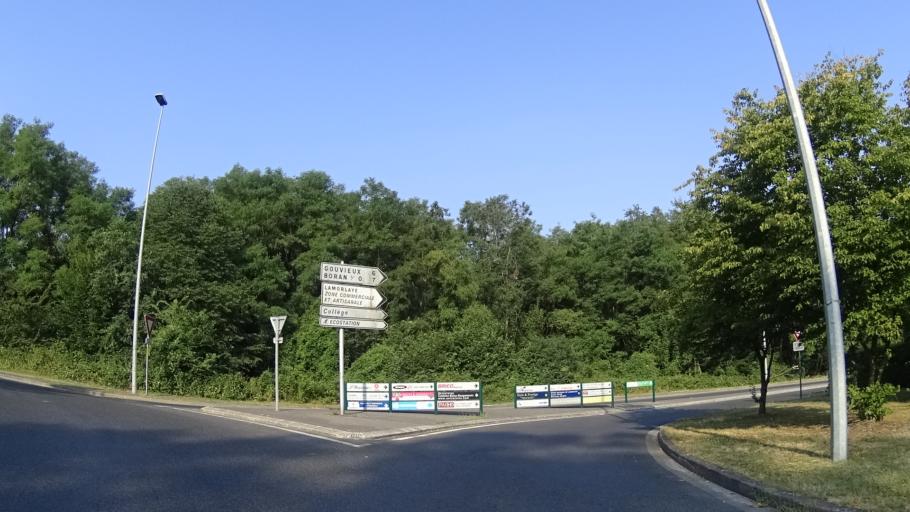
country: FR
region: Picardie
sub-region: Departement de l'Oise
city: Lamorlaye
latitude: 49.1457
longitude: 2.4406
